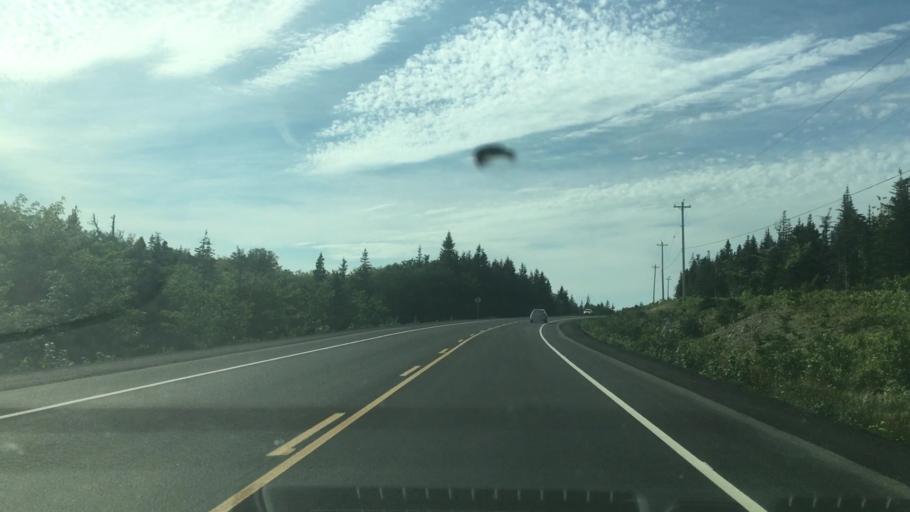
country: CA
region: Nova Scotia
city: Sydney Mines
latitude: 46.8431
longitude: -60.4009
